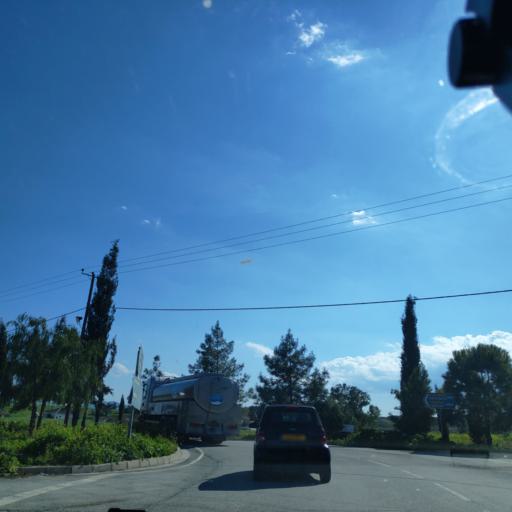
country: CY
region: Lefkosia
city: Tseri
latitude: 35.0237
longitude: 33.3270
